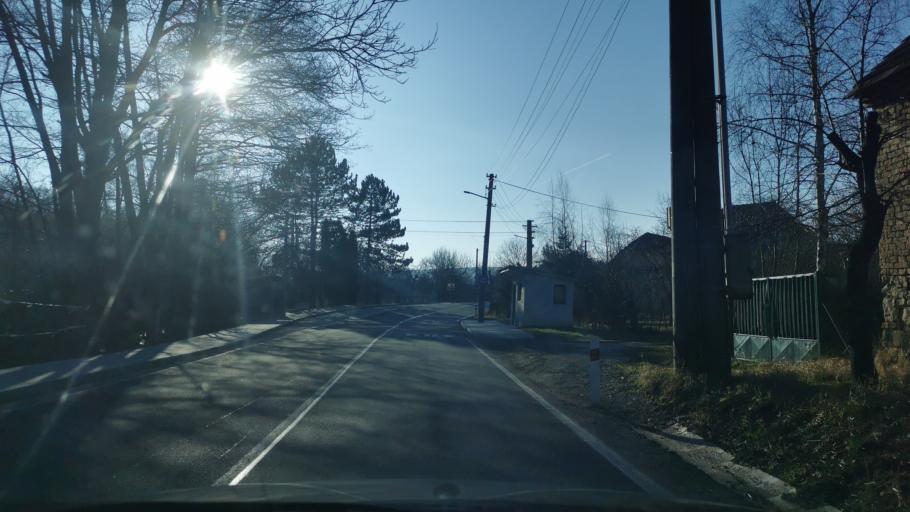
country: SK
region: Trnavsky
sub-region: Okres Senica
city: Senica
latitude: 48.7437
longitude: 17.4492
